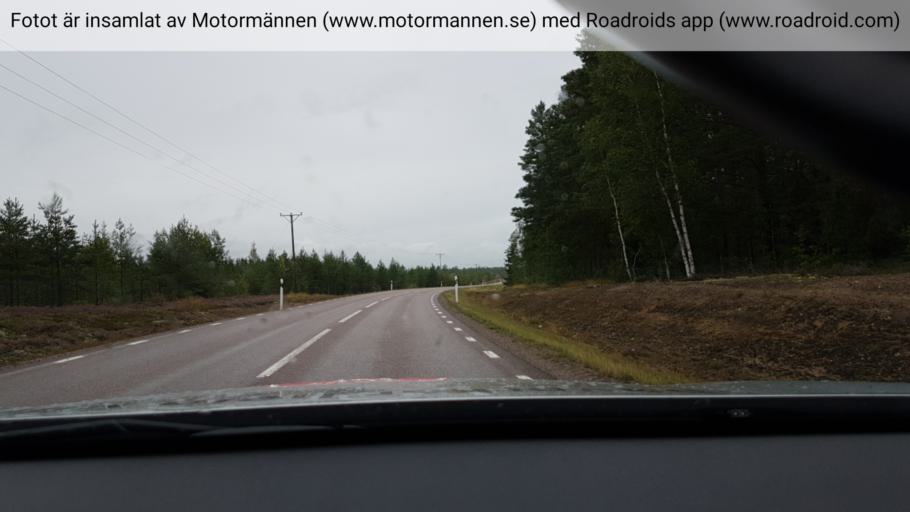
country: SE
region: Gaevleborg
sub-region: Gavle Kommun
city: Valbo
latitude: 60.5432
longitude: 16.9436
